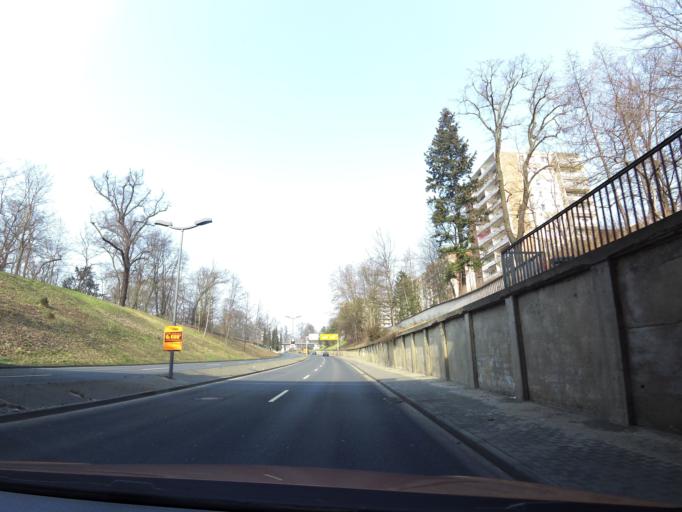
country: DE
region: Brandenburg
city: Frankfurt (Oder)
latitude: 52.3430
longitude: 14.5405
